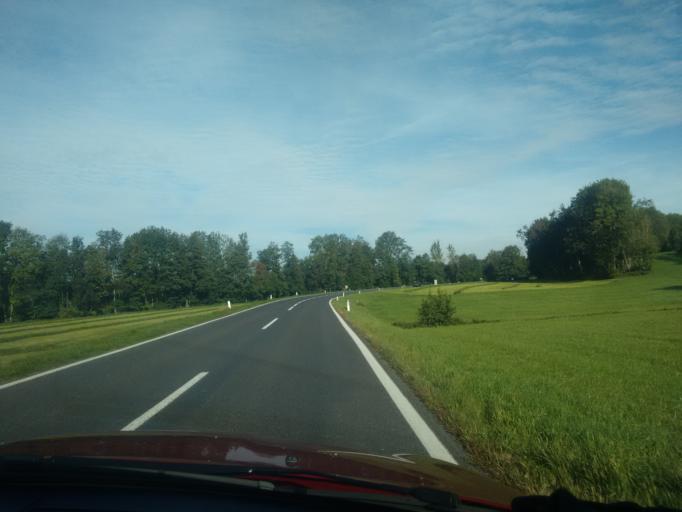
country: AT
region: Upper Austria
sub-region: Politischer Bezirk Vocklabruck
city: Manning
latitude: 48.0732
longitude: 13.6637
